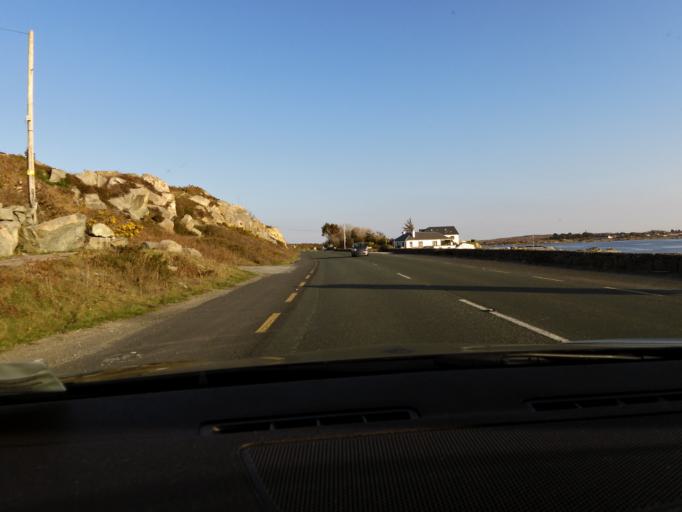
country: IE
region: Connaught
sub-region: County Galway
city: Oughterard
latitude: 53.2870
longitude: -9.5470
